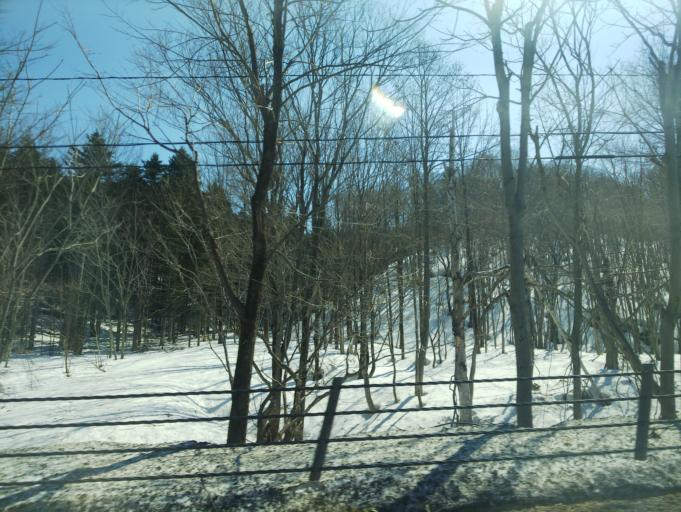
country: JP
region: Hokkaido
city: Nayoro
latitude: 44.7084
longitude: 142.2750
